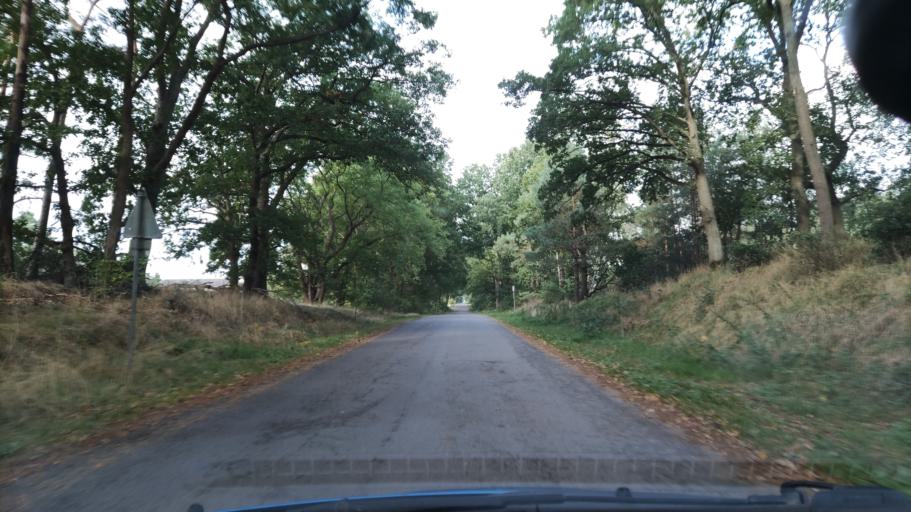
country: DE
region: Lower Saxony
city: Deutsch Evern
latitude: 53.2011
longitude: 10.4510
